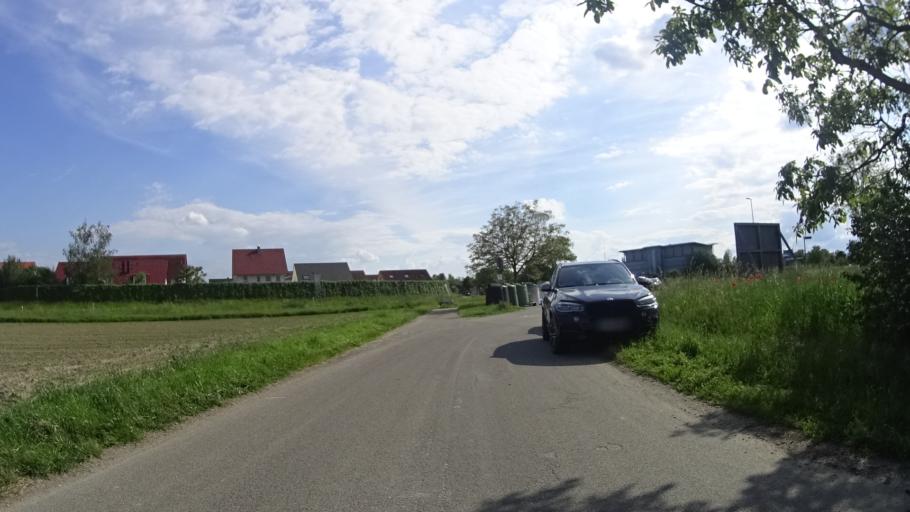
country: DE
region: Baden-Wuerttemberg
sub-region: Freiburg Region
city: Breisach am Rhein
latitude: 48.0445
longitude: 7.5817
